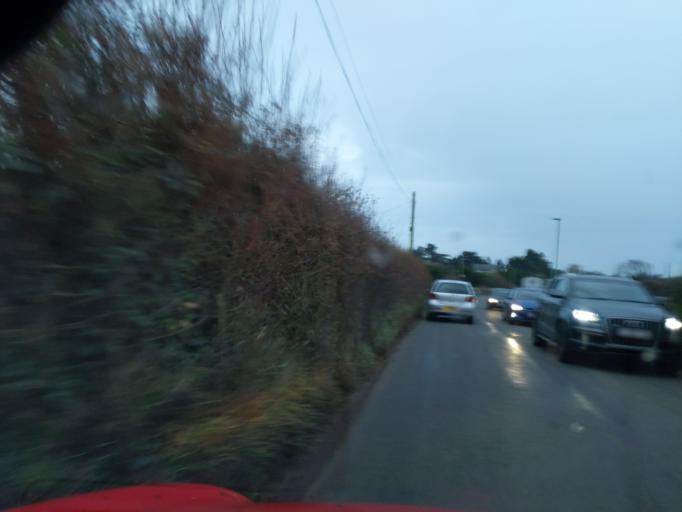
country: GB
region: England
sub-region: Devon
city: Wembury
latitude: 50.3419
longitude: -4.0746
